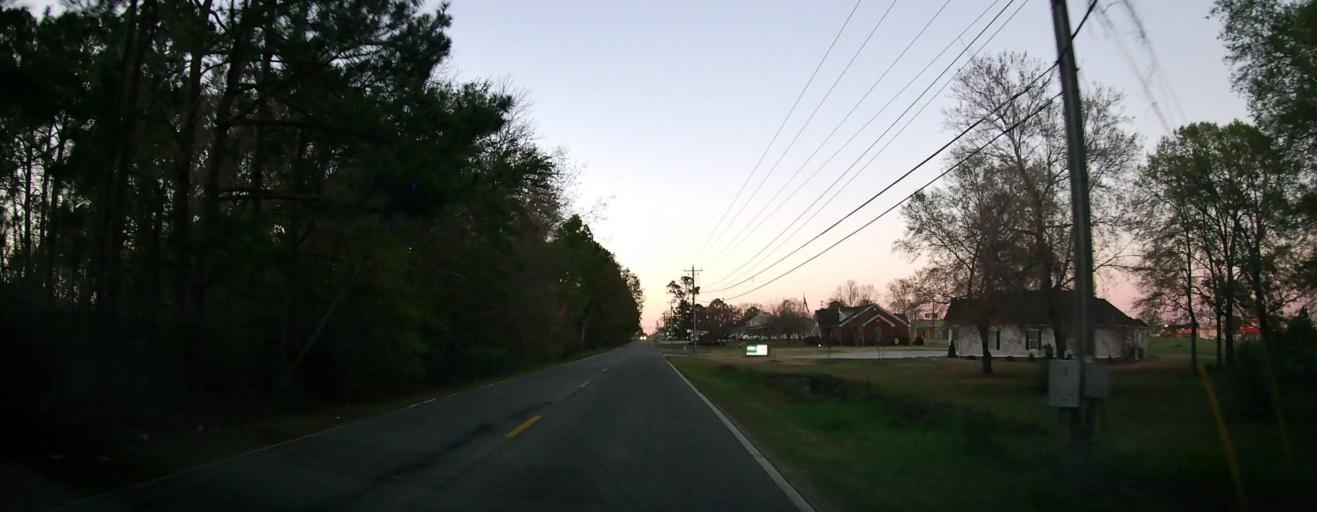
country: US
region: Georgia
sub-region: Crisp County
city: Cordele
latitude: 31.9552
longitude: -83.7561
